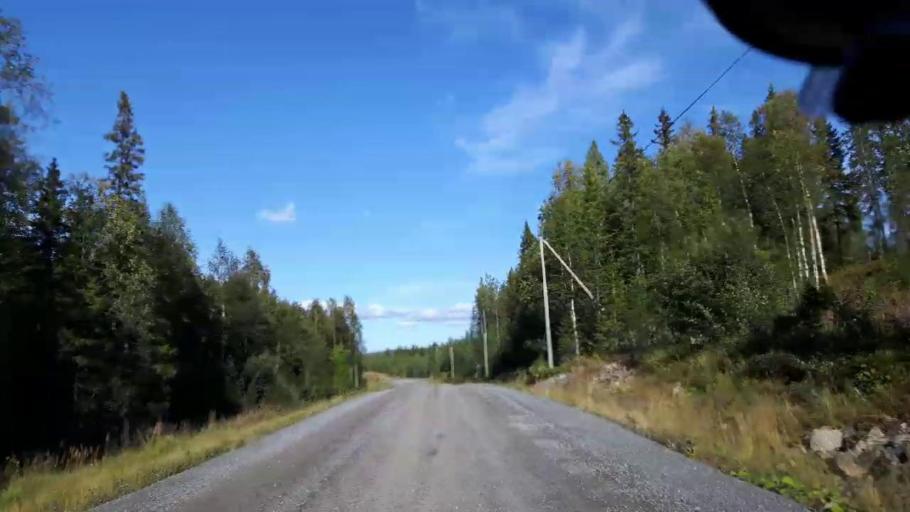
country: SE
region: Jaemtland
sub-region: Ragunda Kommun
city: Hammarstrand
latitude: 63.4424
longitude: 16.2021
